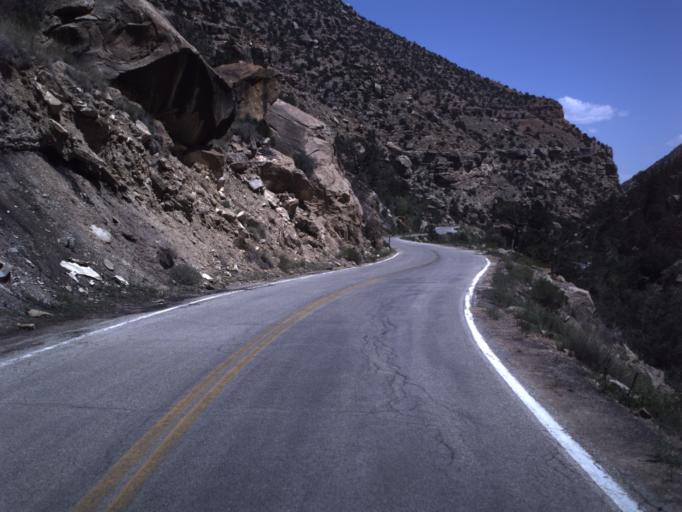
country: US
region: Utah
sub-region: Emery County
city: Orangeville
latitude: 39.2747
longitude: -111.2133
